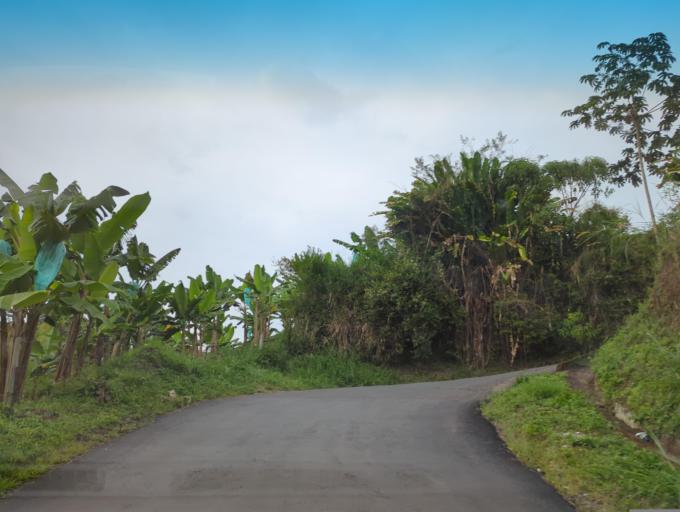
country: CO
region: Risaralda
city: Pereira
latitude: 4.8259
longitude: -75.7586
